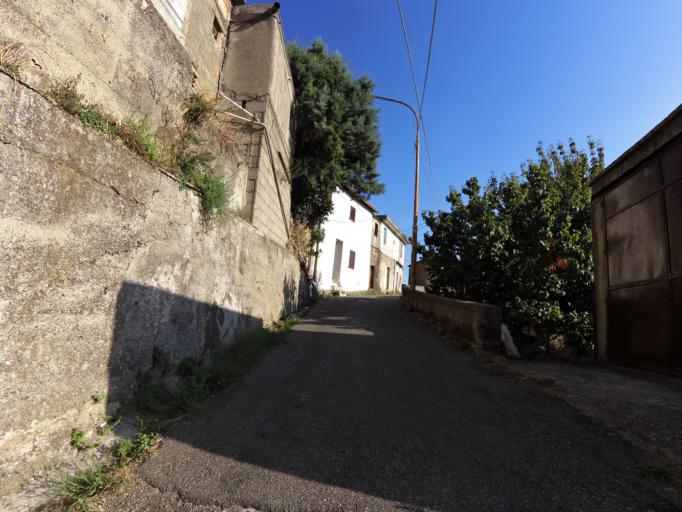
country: IT
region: Calabria
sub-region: Provincia di Reggio Calabria
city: Pazzano
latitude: 38.4504
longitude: 16.4126
